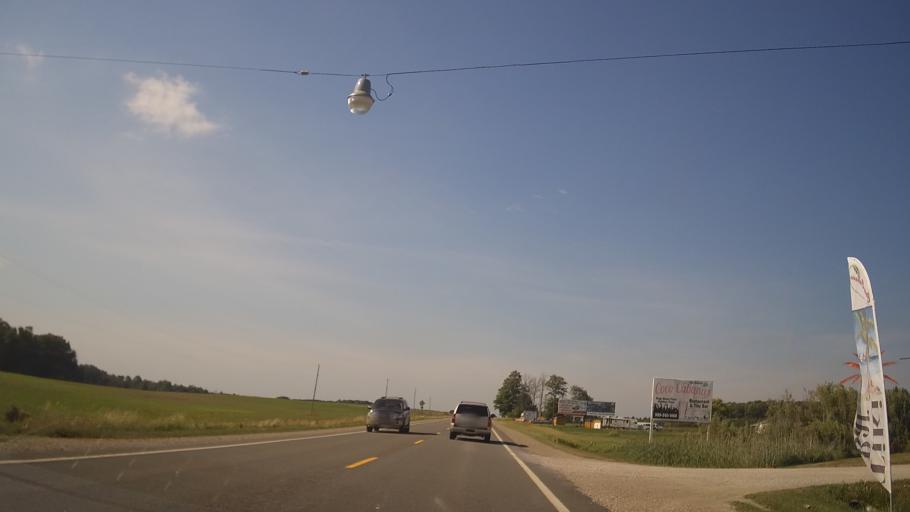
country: US
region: Michigan
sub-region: Ogemaw County
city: West Branch
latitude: 44.2663
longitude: -84.1257
